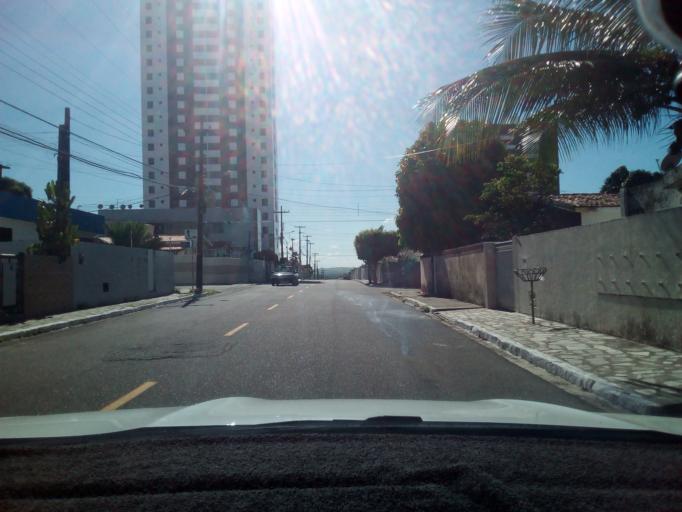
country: BR
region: Paraiba
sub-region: Joao Pessoa
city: Joao Pessoa
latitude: -7.1095
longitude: -34.8647
